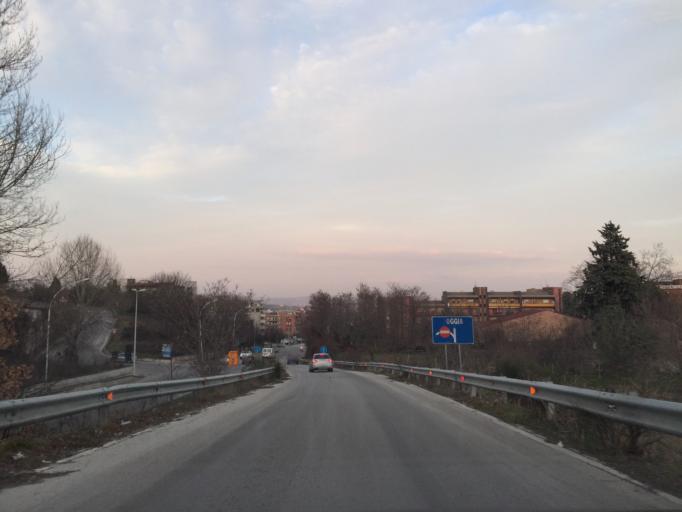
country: IT
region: Molise
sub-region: Provincia di Campobasso
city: Campobasso
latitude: 41.5585
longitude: 14.6770
